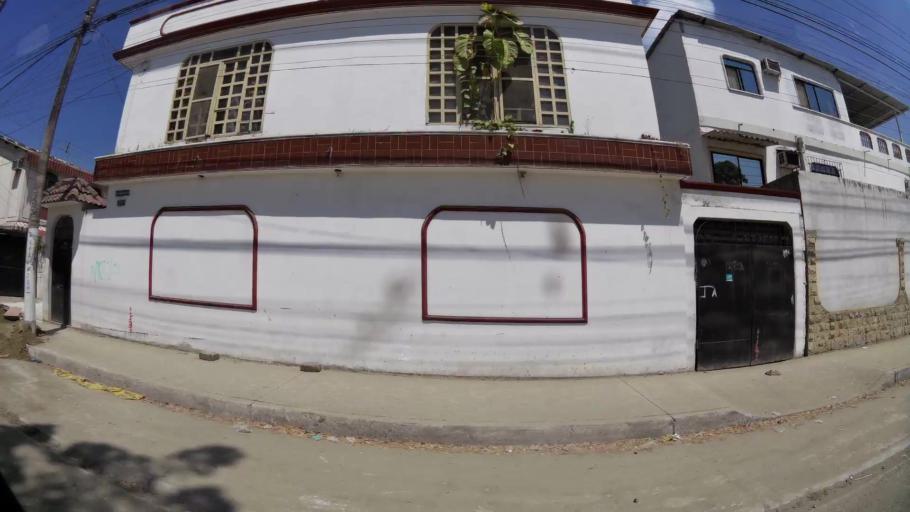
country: EC
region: Guayas
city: Eloy Alfaro
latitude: -2.1133
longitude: -79.9023
